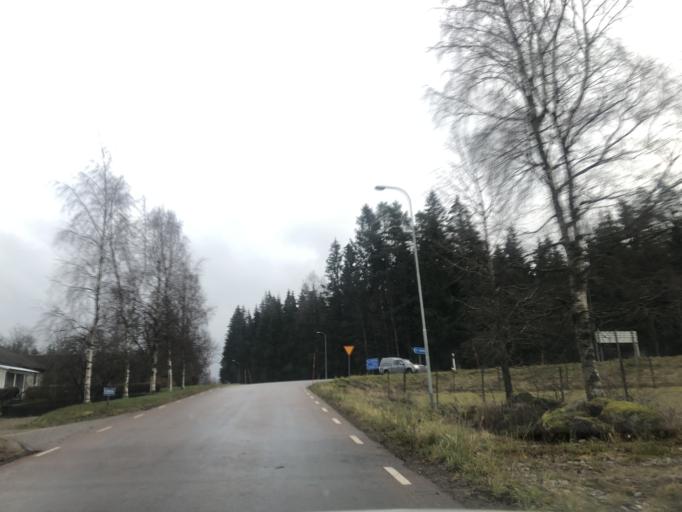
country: SE
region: Vaestra Goetaland
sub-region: Ulricehamns Kommun
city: Ulricehamn
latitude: 57.8252
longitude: 13.5158
